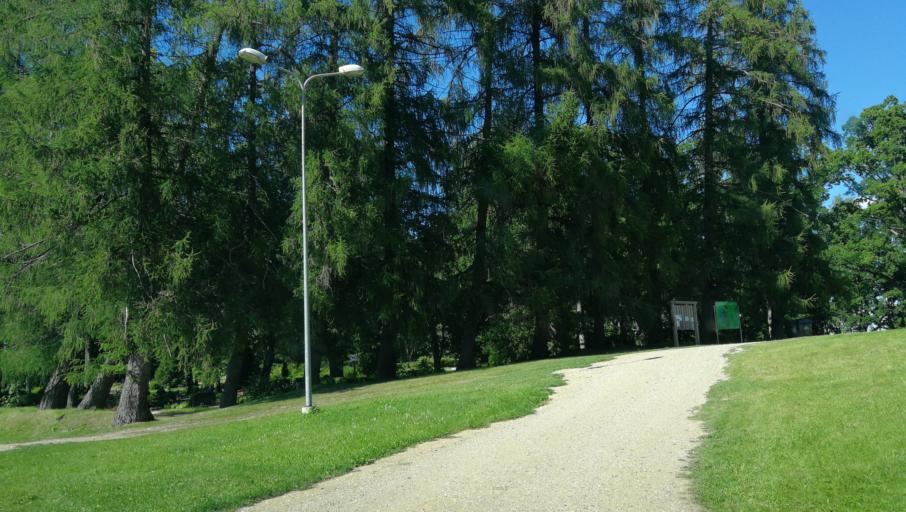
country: LV
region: Cesvaine
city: Cesvaine
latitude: 56.9718
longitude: 26.3043
